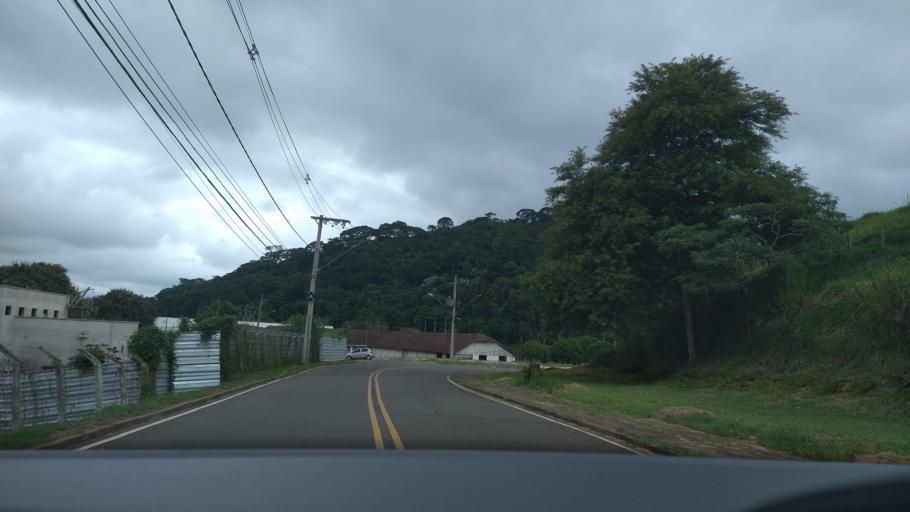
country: BR
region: Minas Gerais
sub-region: Vicosa
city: Vicosa
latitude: -20.7685
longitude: -42.8620
